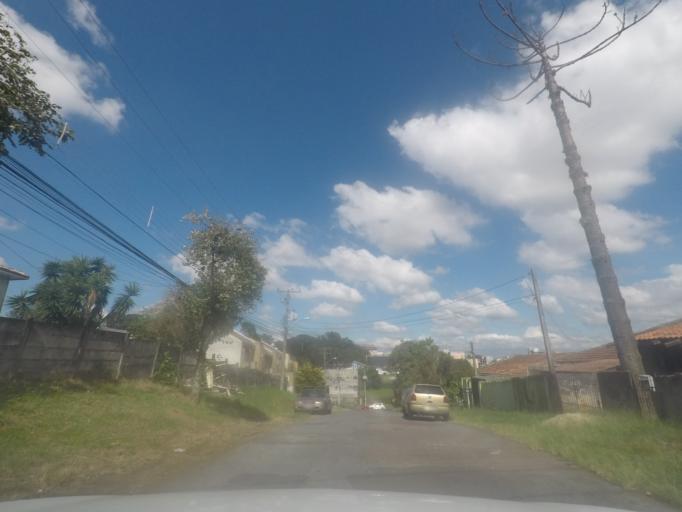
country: BR
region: Parana
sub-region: Pinhais
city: Pinhais
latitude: -25.4823
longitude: -49.2196
